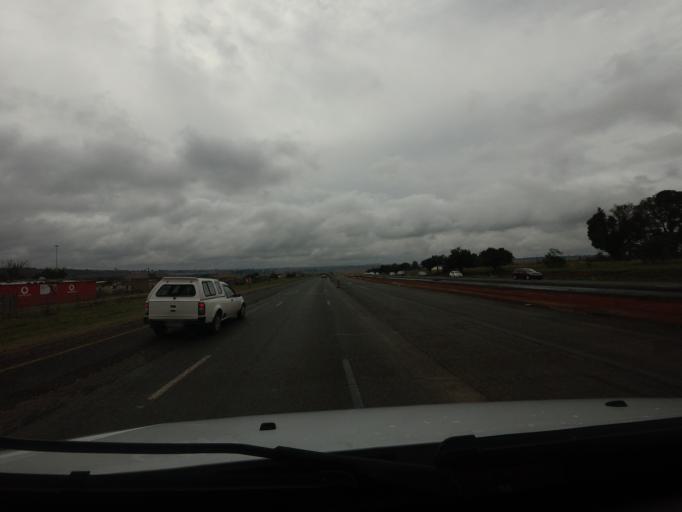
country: ZA
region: Mpumalanga
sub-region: Nkangala District Municipality
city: Witbank
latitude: -25.8746
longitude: 29.1441
